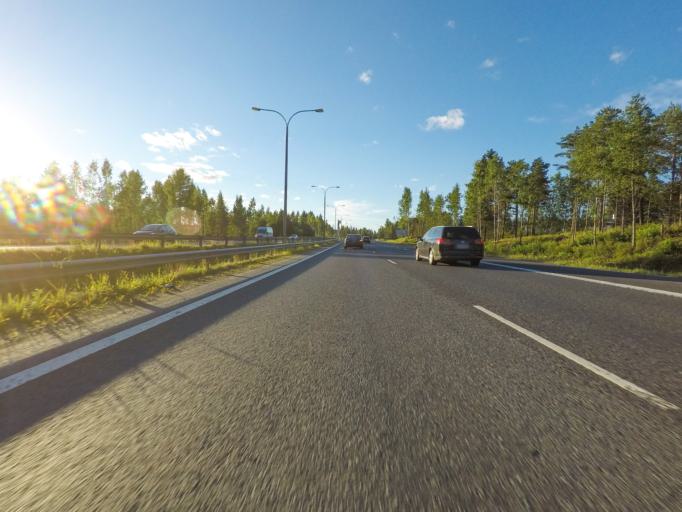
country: FI
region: Northern Savo
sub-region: Kuopio
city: Kuopio
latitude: 62.8550
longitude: 27.6212
